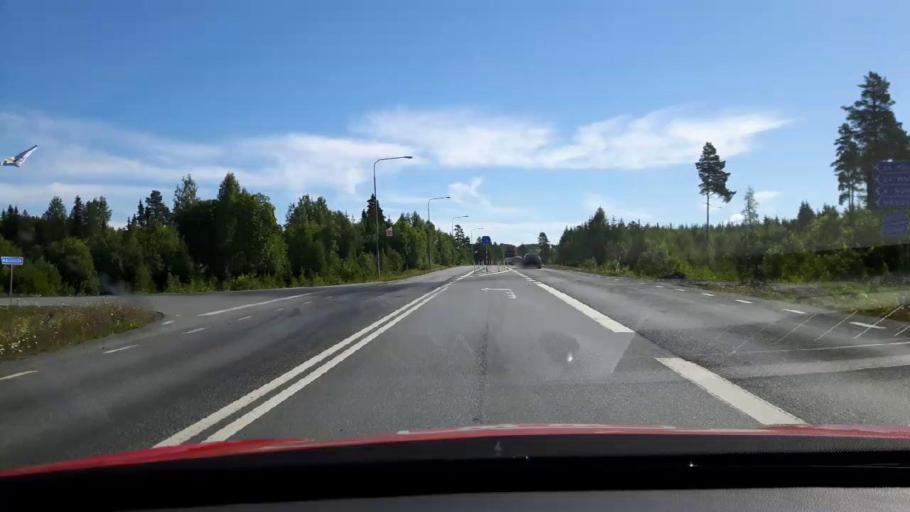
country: SE
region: Jaemtland
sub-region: OEstersunds Kommun
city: Lit
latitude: 63.3898
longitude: 14.9071
